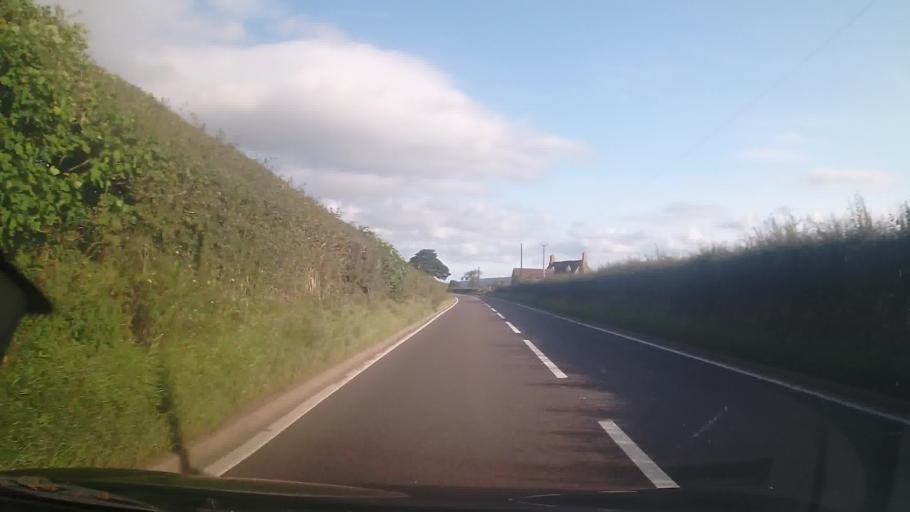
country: GB
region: England
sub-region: Shropshire
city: Bromfield
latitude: 52.4013
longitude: -2.7999
